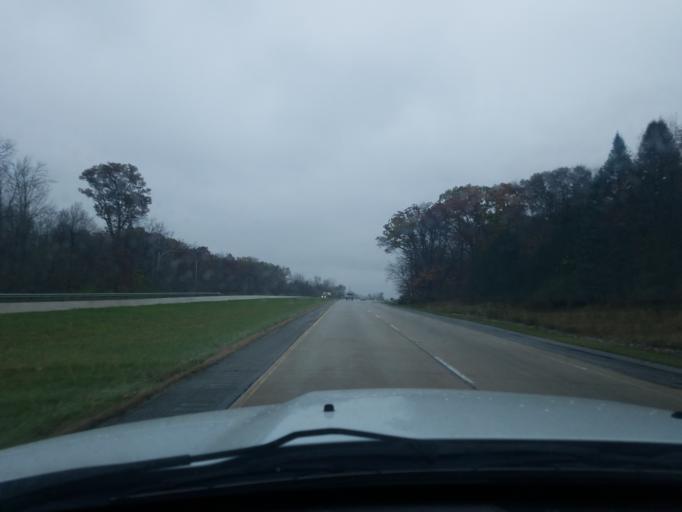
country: US
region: Indiana
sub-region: Cass County
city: Logansport
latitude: 40.7319
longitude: -86.3172
